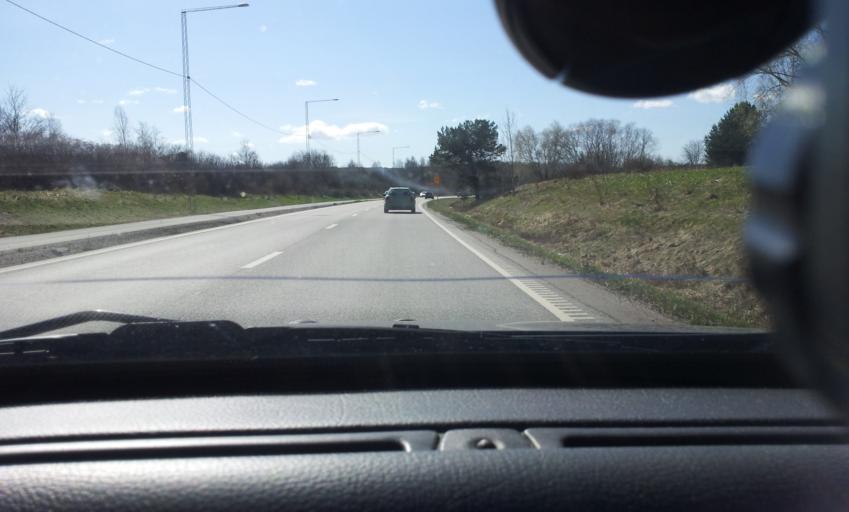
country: SE
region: Stockholm
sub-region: Haninge Kommun
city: Haninge
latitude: 59.1852
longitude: 18.1716
